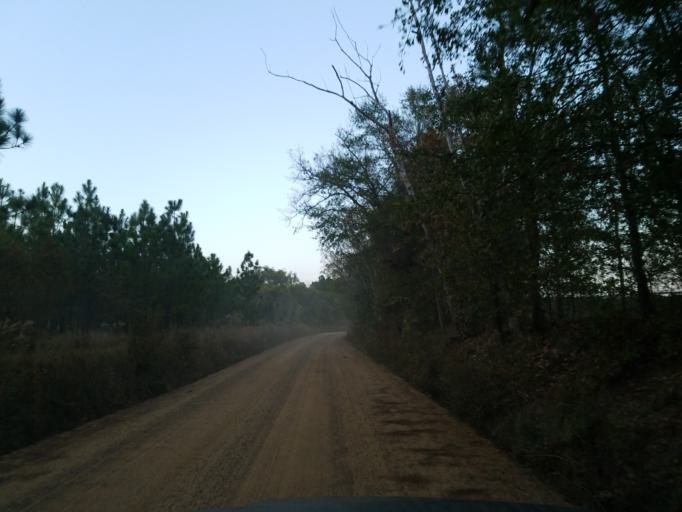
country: US
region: Georgia
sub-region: Turner County
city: Ashburn
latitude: 31.7332
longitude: -83.4842
